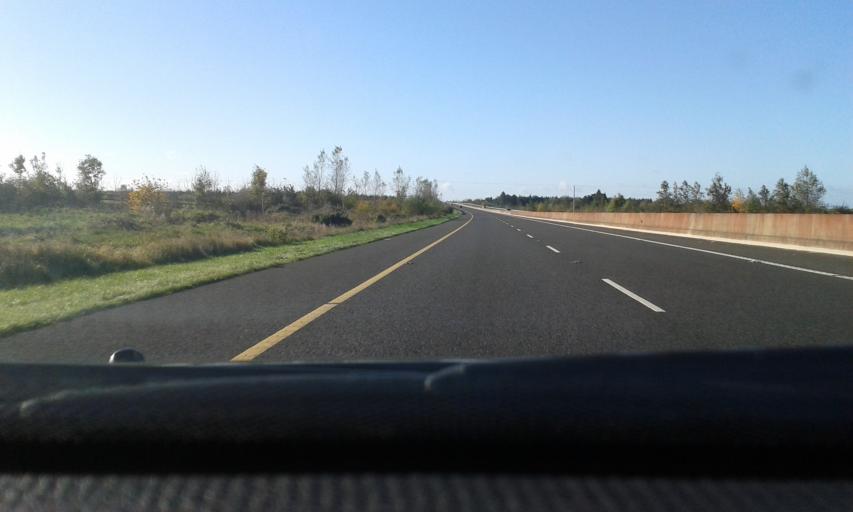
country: IE
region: Leinster
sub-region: Laois
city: Rathdowney
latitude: 52.7071
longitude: -7.6299
